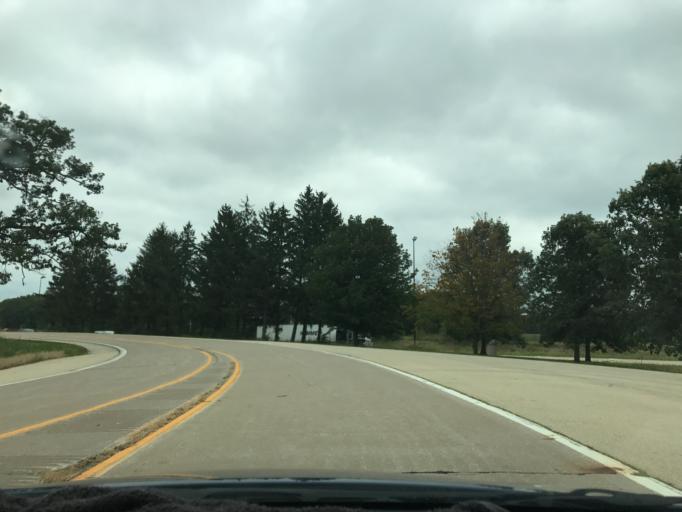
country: US
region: Iowa
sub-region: Scott County
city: Le Claire
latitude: 41.5666
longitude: -90.3558
